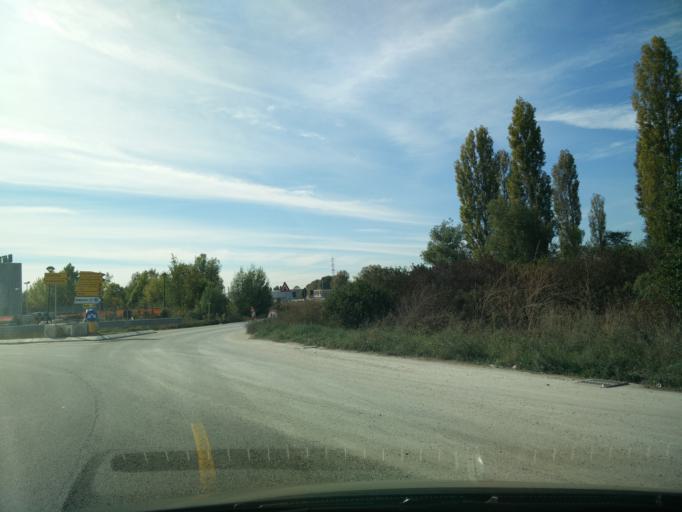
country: IT
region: Veneto
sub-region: Provincia di Venezia
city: Mestre
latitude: 45.4442
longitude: 12.2120
